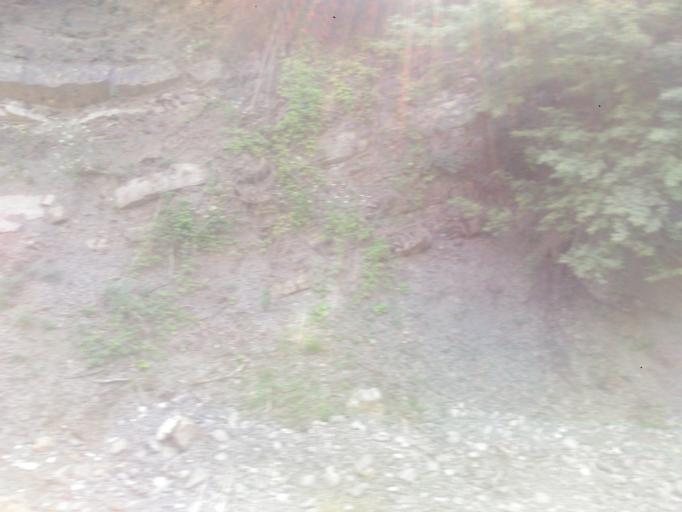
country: GE
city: Zhinvali
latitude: 42.1901
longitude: 44.8229
